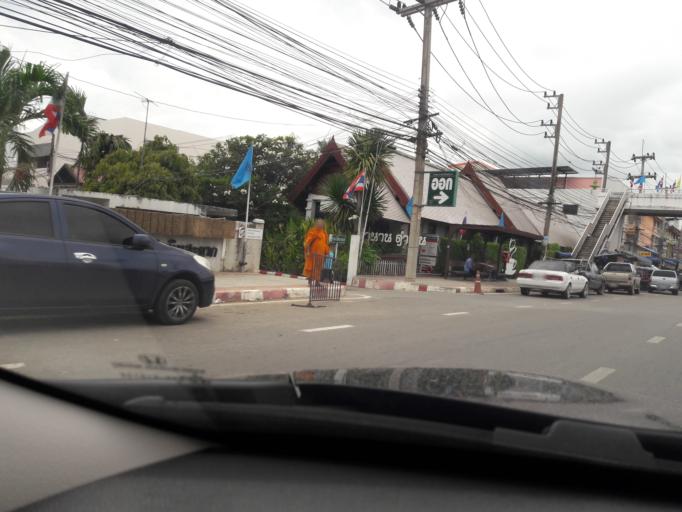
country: TH
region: Ratchaburi
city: Damnoen Saduak
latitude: 13.5357
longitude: 99.9654
